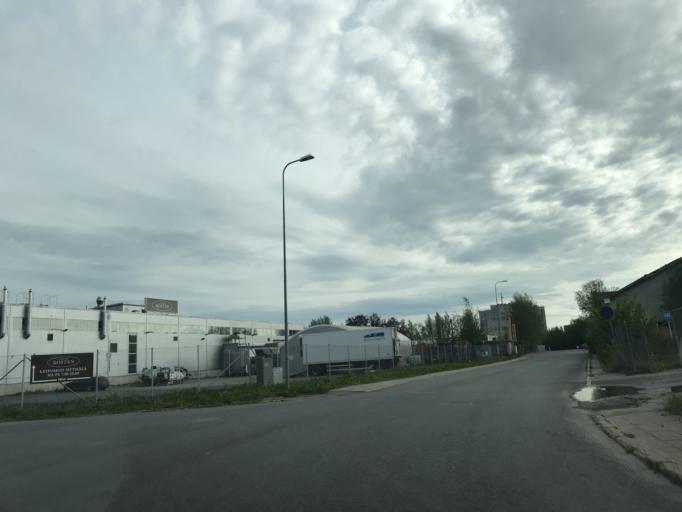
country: FI
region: Varsinais-Suomi
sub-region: Turku
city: Turku
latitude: 60.4488
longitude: 22.3080
